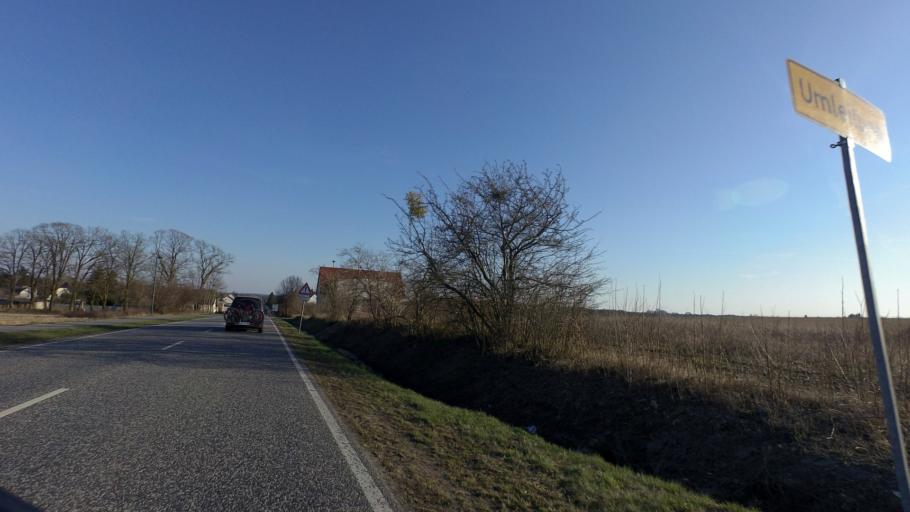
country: DE
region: Brandenburg
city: Britz
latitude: 52.8813
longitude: 13.8159
